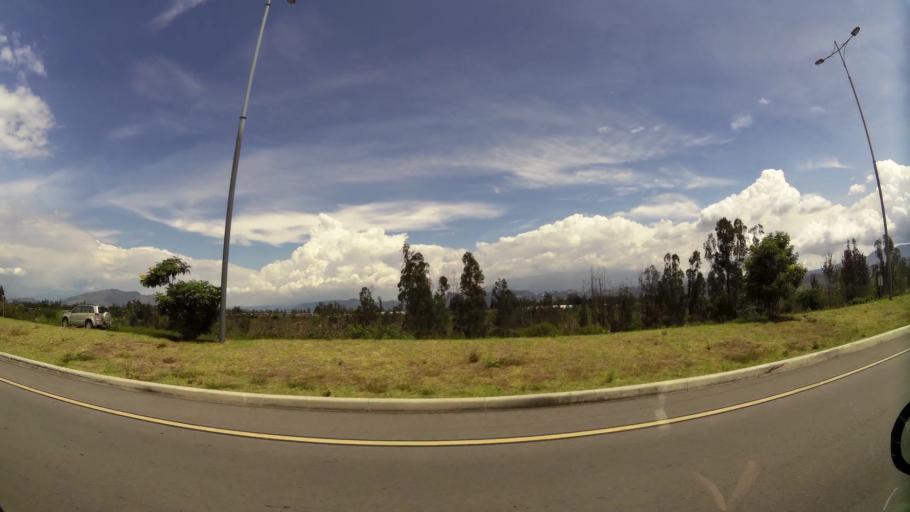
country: EC
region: Pichincha
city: Quito
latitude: -0.1463
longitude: -78.3547
